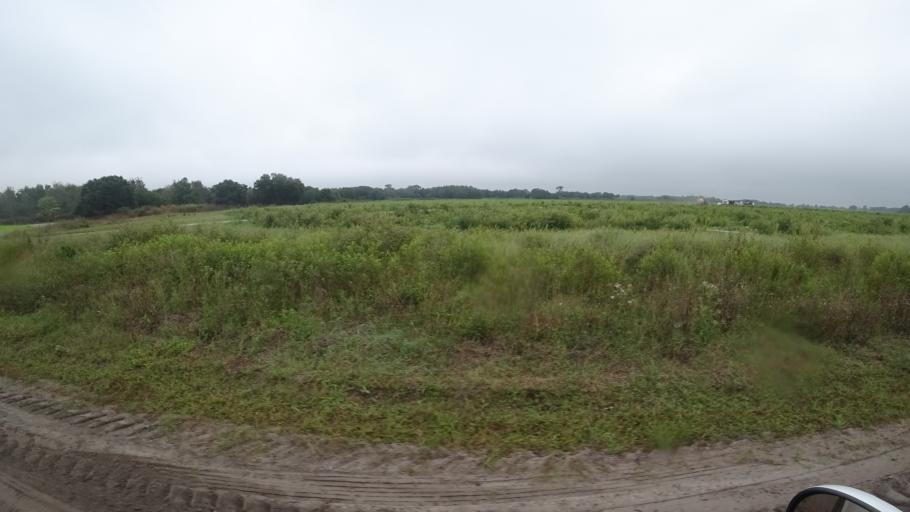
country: US
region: Florida
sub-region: Sarasota County
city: Warm Mineral Springs
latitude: 27.2835
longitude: -82.1653
